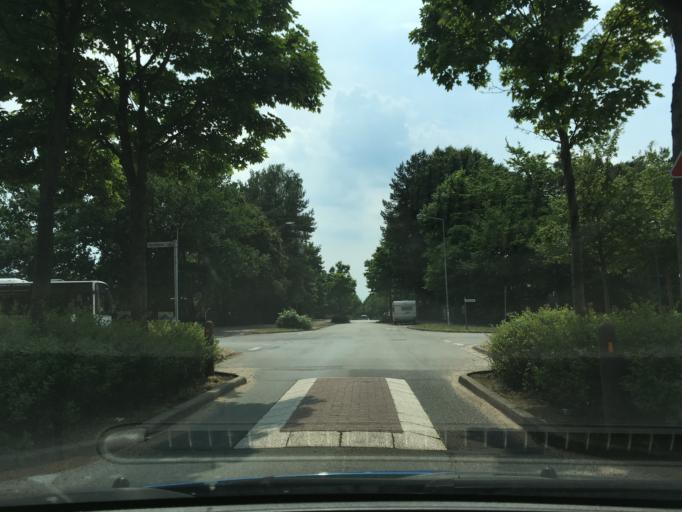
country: DE
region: Lower Saxony
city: Buchholz in der Nordheide
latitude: 53.3386
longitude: 9.8877
